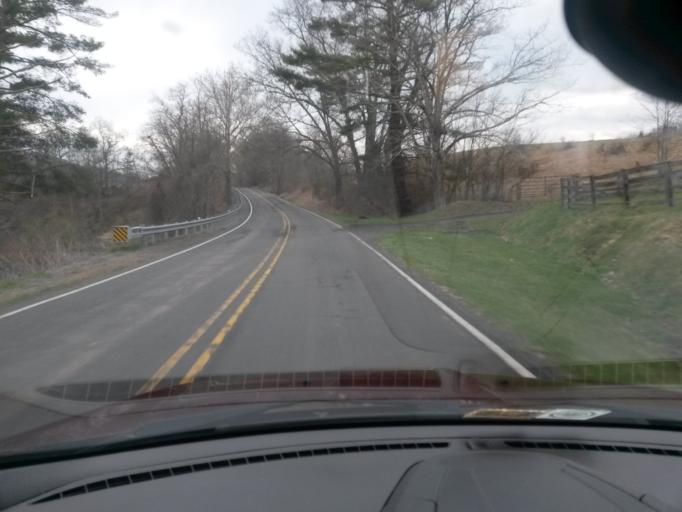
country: US
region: Virginia
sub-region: Bath County
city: Warm Springs
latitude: 38.1953
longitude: -79.7317
